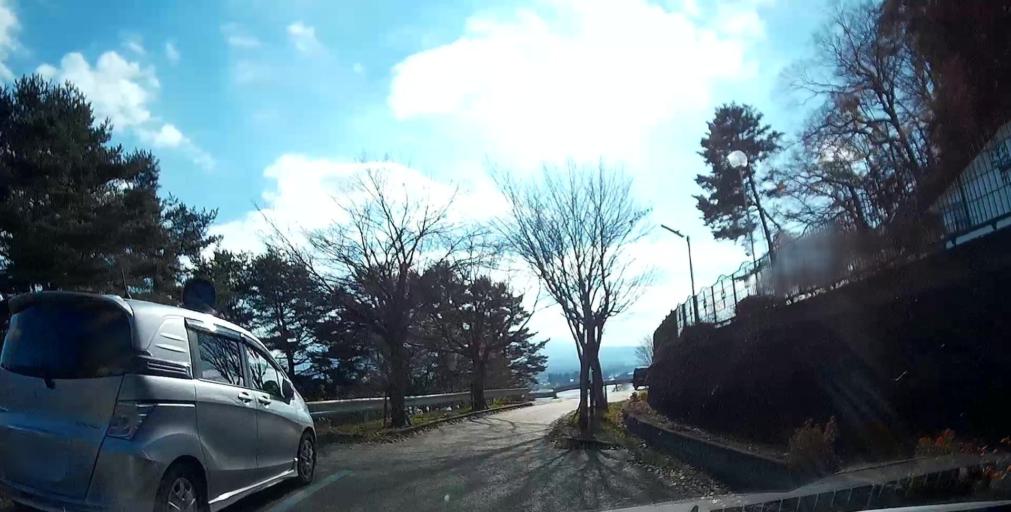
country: JP
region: Yamanashi
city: Fujikawaguchiko
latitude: 35.5221
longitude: 138.7575
